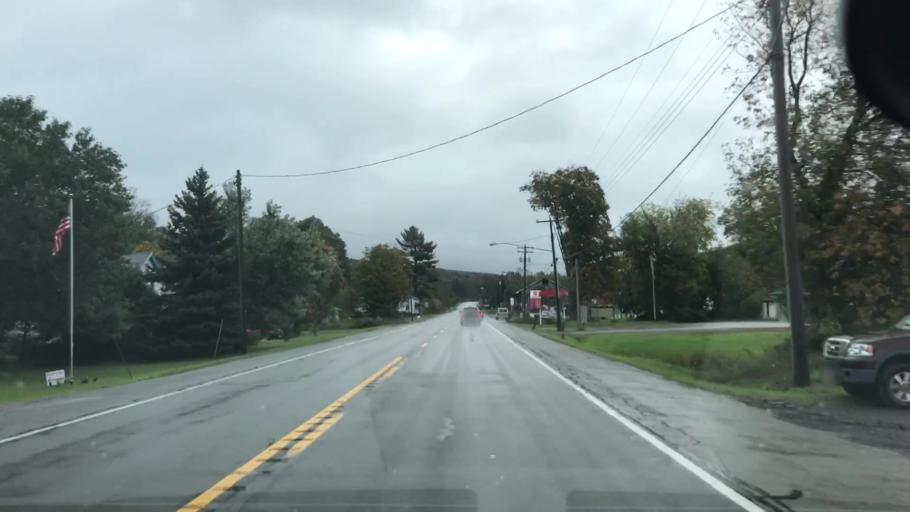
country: US
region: New York
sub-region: Erie County
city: Springville
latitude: 42.4025
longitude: -78.6843
